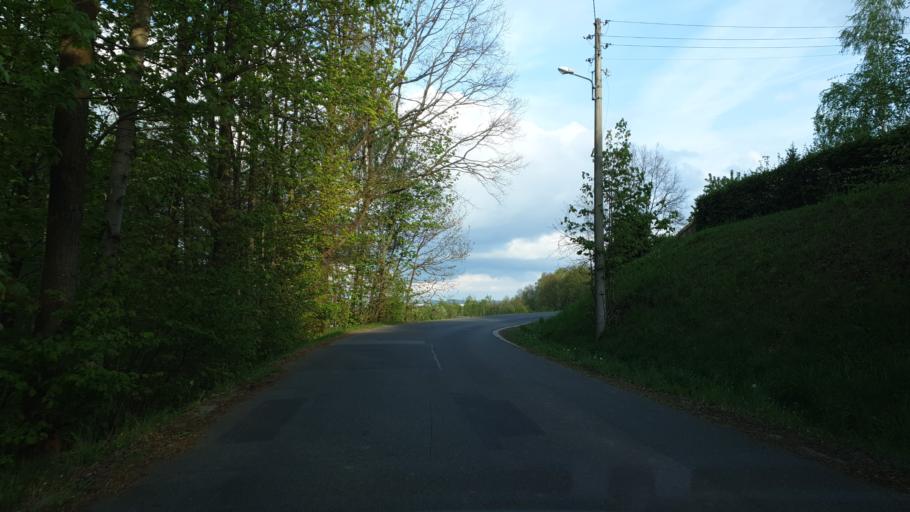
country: DE
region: Saxony
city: Oelsnitz
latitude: 50.7319
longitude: 12.6889
